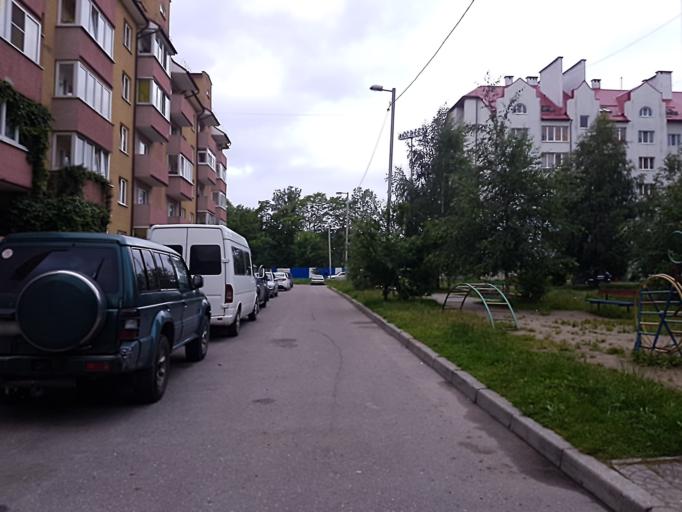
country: RU
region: Kaliningrad
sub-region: Gorod Kaliningrad
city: Kaliningrad
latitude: 54.6903
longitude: 20.5211
